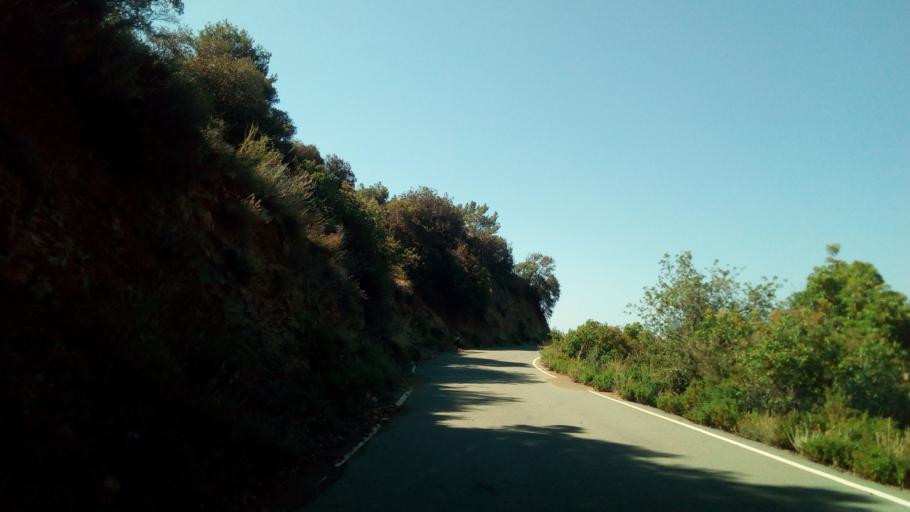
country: CY
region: Lefkosia
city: Lythrodontas
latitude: 34.8891
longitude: 33.2199
